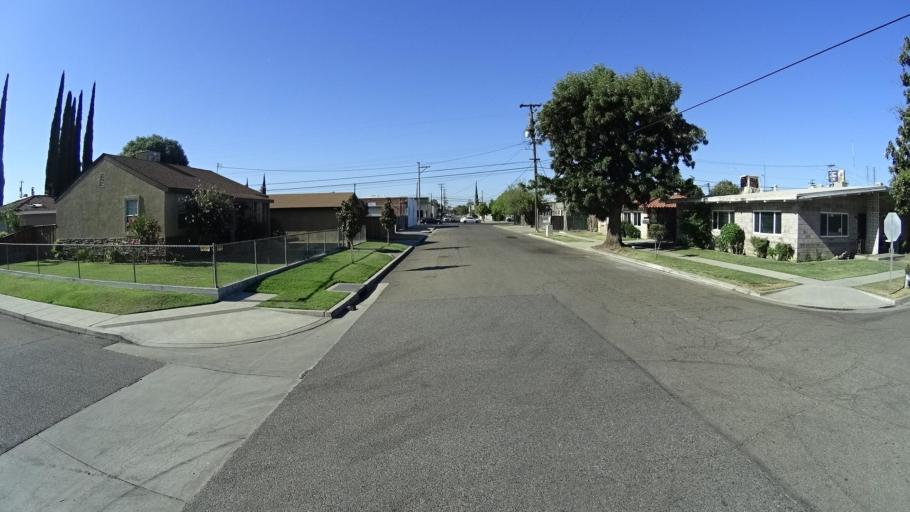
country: US
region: California
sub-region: Fresno County
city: Fresno
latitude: 36.7660
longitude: -119.7838
